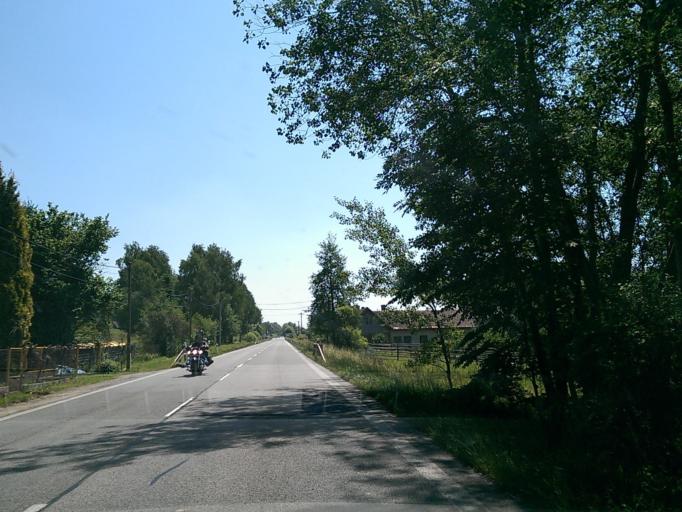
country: CZ
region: Liberecky
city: Rovensko pod Troskami
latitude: 50.5400
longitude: 15.2272
